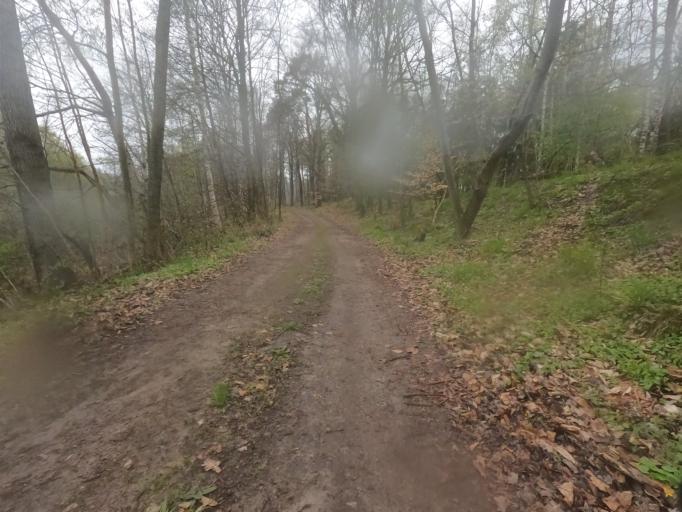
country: PL
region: West Pomeranian Voivodeship
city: Trzcinsko Zdroj
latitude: 52.9270
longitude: 14.7109
